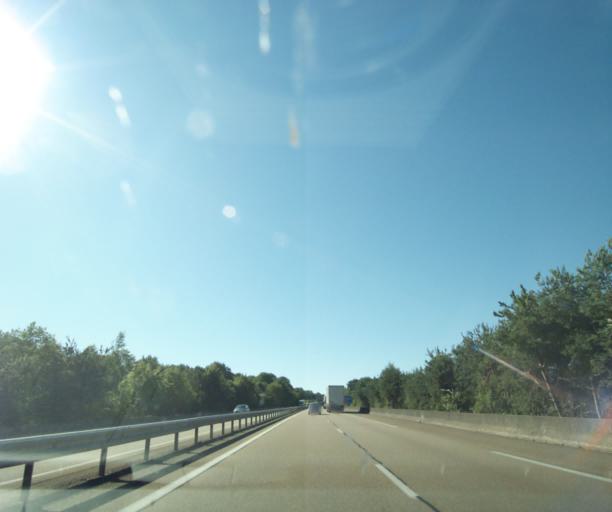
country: FR
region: Champagne-Ardenne
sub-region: Departement de la Haute-Marne
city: Chamarandes-Choignes
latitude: 48.0250
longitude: 5.0909
